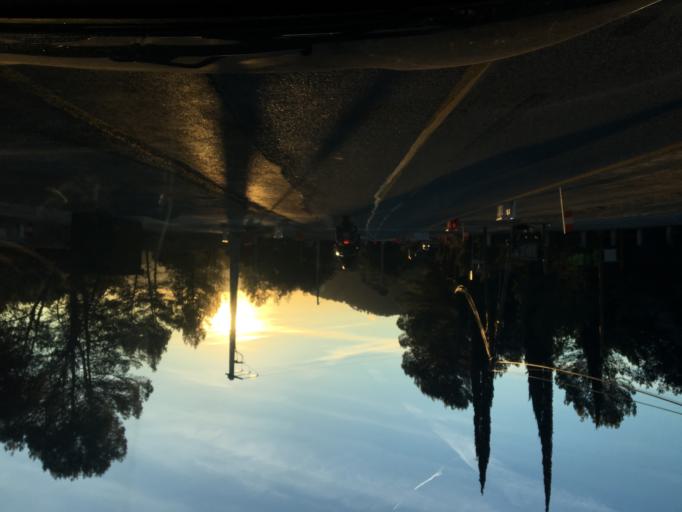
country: FR
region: Provence-Alpes-Cote d'Azur
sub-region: Departement du Var
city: Taradeau
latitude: 43.4603
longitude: 6.4162
